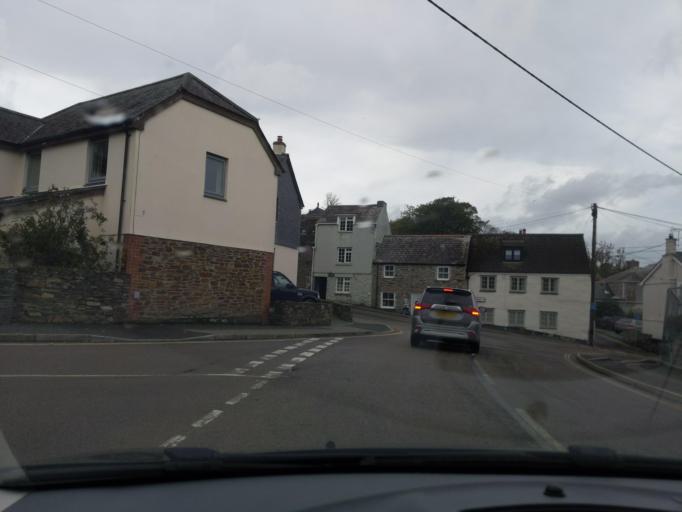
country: GB
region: England
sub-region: Cornwall
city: Padstow
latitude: 50.5396
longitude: -4.9384
